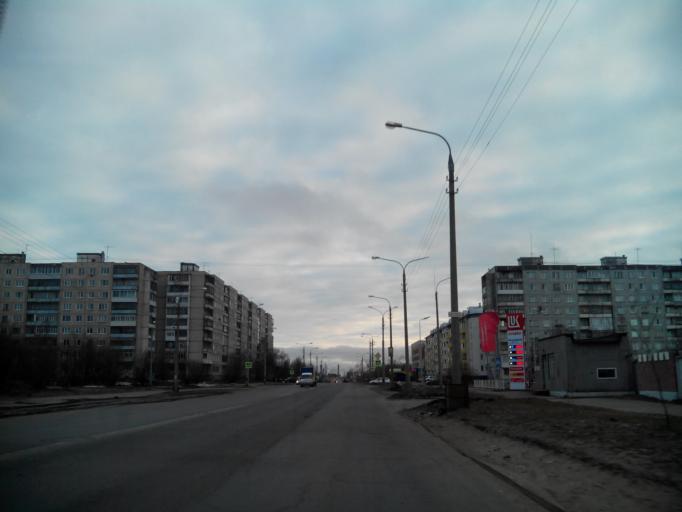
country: RU
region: Arkhangelskaya
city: Arkhangel'sk
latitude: 64.5158
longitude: 40.6724
